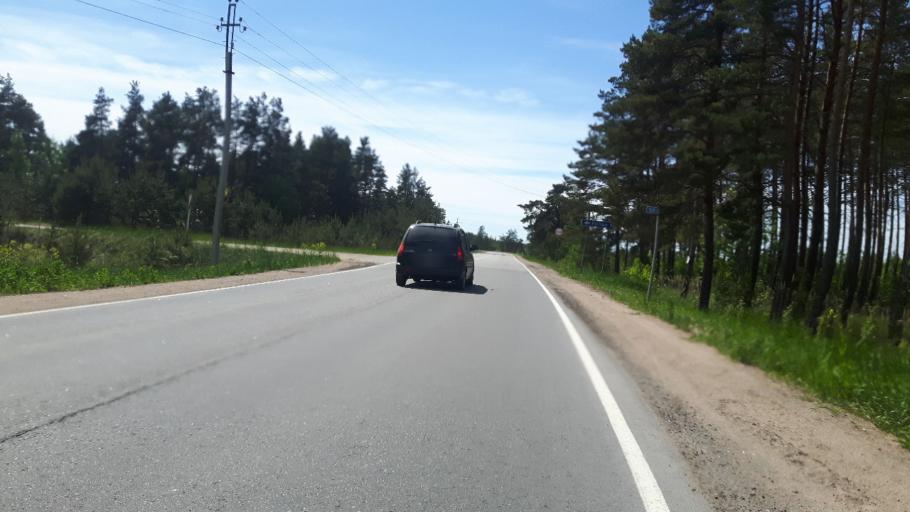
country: RU
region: Leningrad
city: Ust'-Luga
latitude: 59.5712
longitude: 28.1587
